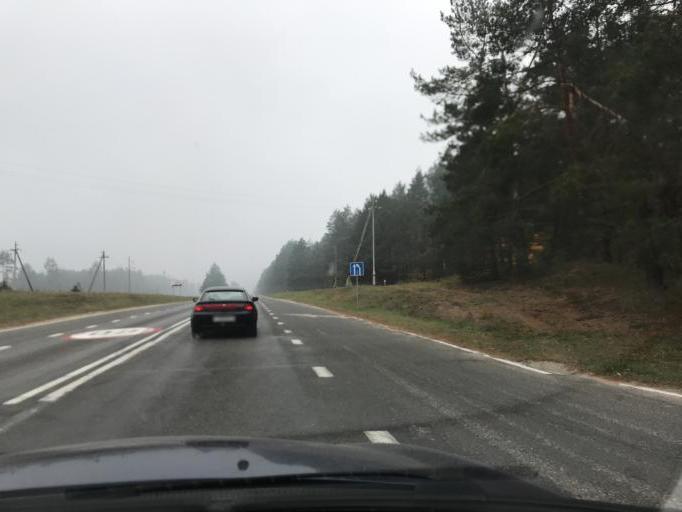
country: BY
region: Grodnenskaya
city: Hrodna
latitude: 53.8049
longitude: 23.8603
